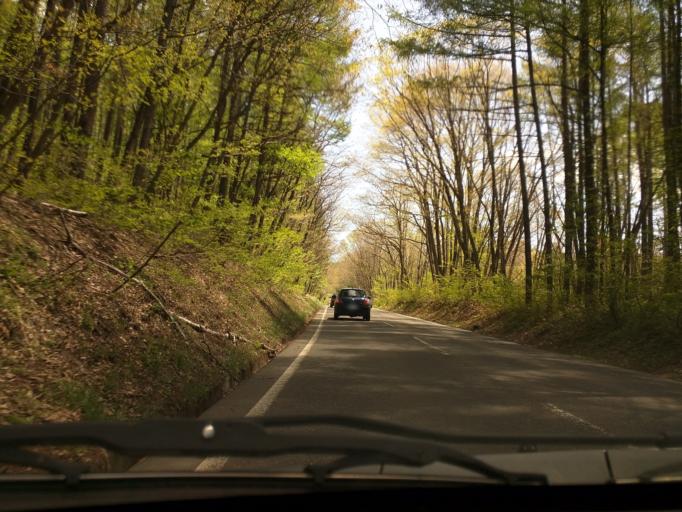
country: JP
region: Nagano
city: Nagano-shi
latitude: 36.7161
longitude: 138.1084
